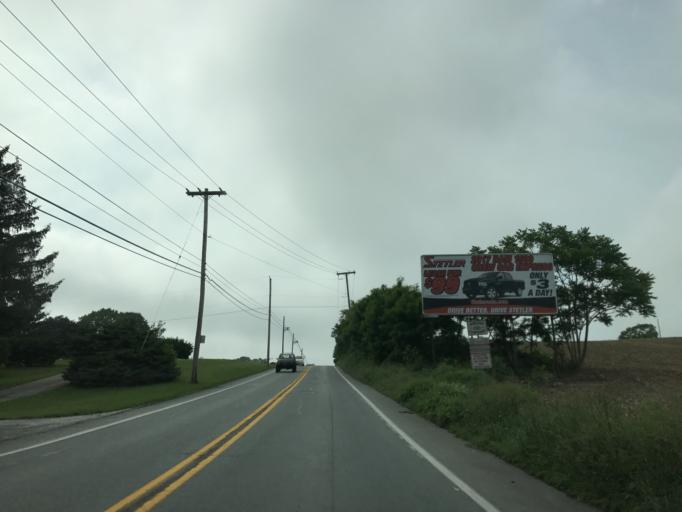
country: US
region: Pennsylvania
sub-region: York County
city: Windsor
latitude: 39.8840
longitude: -76.5420
